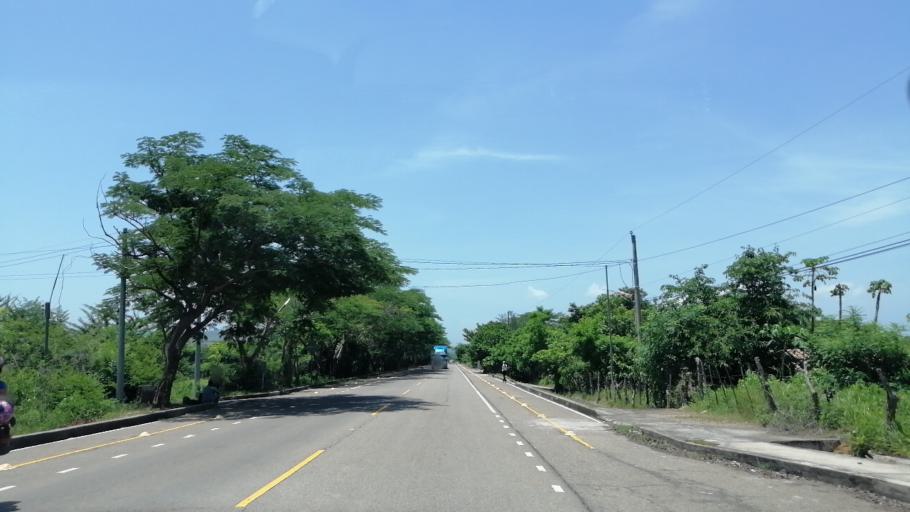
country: SV
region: Chalatenango
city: Nueva Concepcion
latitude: 14.1459
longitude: -89.3034
